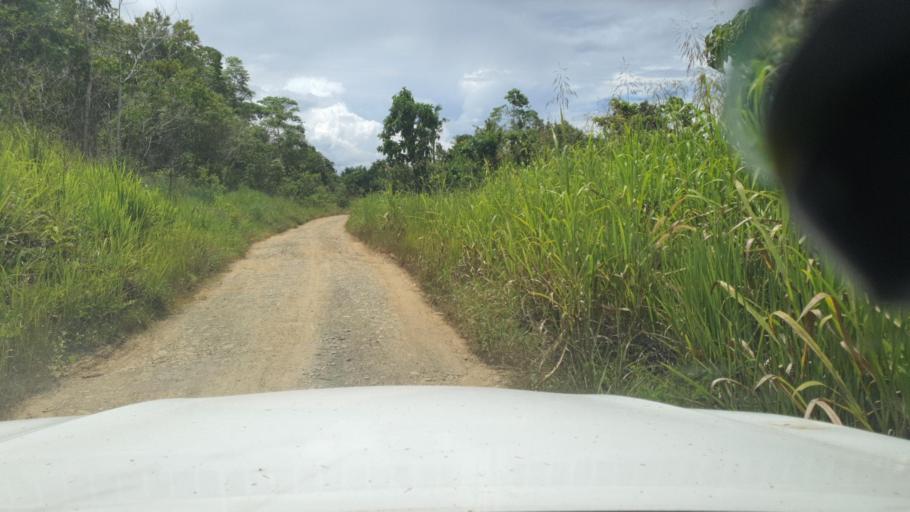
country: SB
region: Guadalcanal
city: Honiara
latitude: -9.4855
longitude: 160.3308
